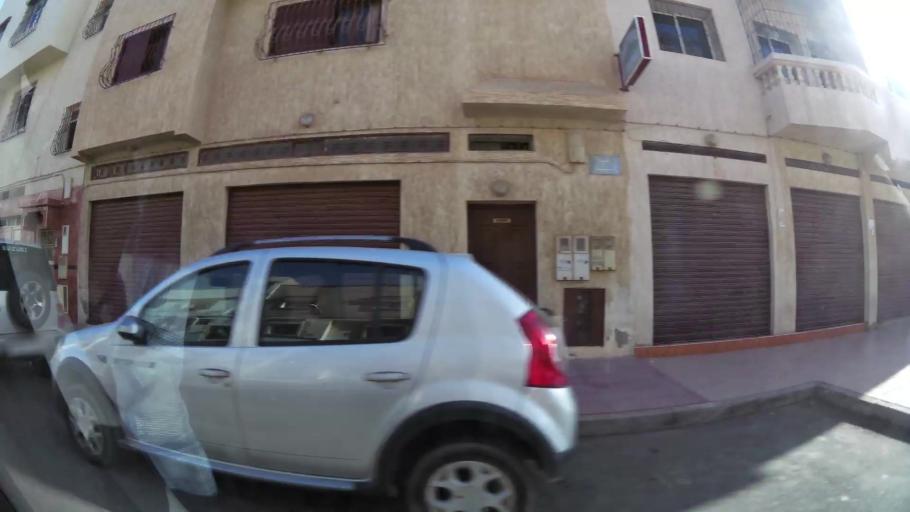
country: MA
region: Oued ed Dahab-Lagouira
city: Dakhla
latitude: 30.4022
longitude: -9.5542
